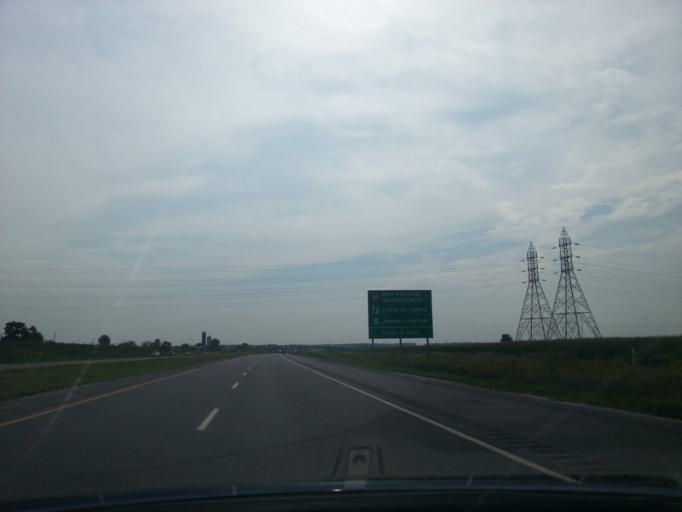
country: CA
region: Quebec
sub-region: Monteregie
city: Notre-Dame-de-l'Ile-Perrot
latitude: 45.3020
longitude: -73.9698
